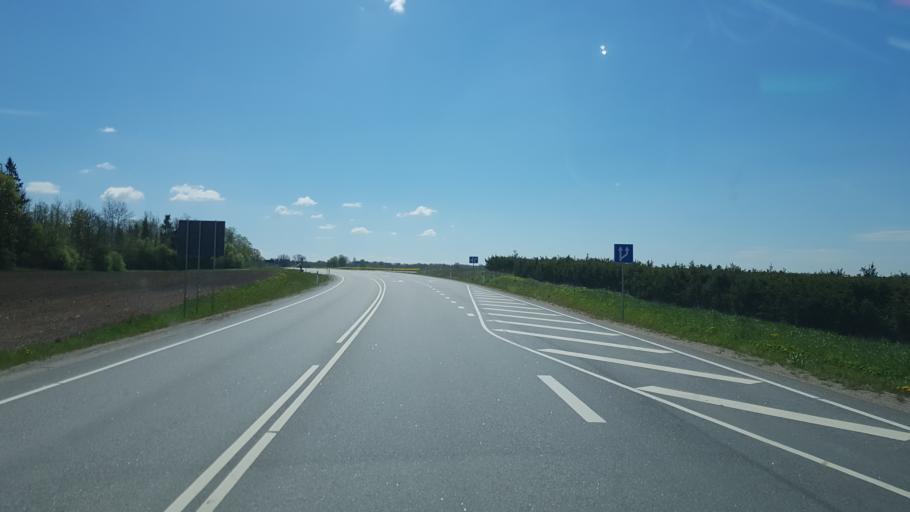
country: EE
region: Viljandimaa
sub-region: Viiratsi vald
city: Viiratsi
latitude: 58.3417
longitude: 25.6281
